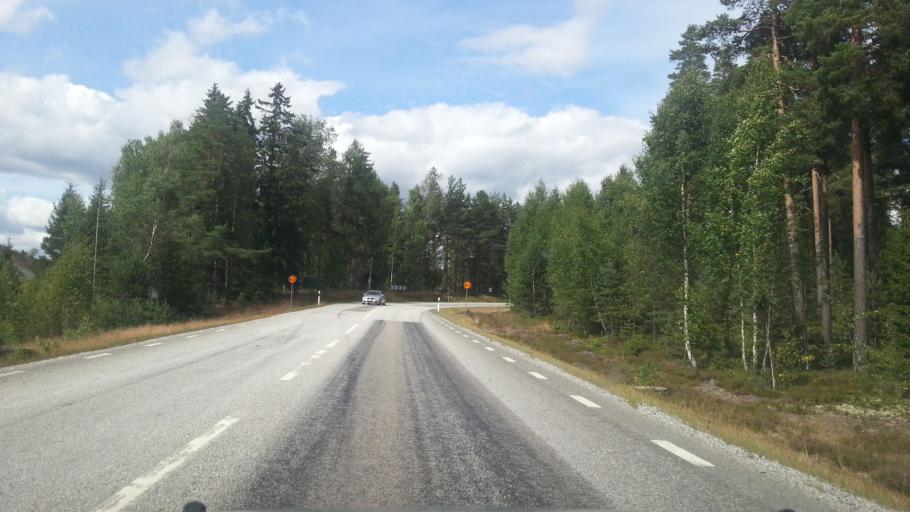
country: SE
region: Vaestmanland
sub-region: Skinnskattebergs Kommun
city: Skinnskatteberg
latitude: 59.8055
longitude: 15.5446
